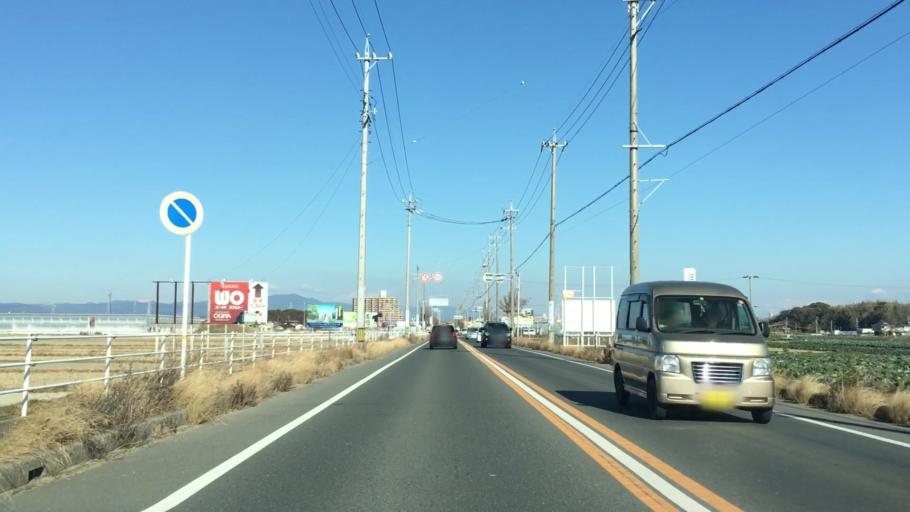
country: JP
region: Aichi
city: Toyohashi
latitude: 34.7323
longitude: 137.3596
